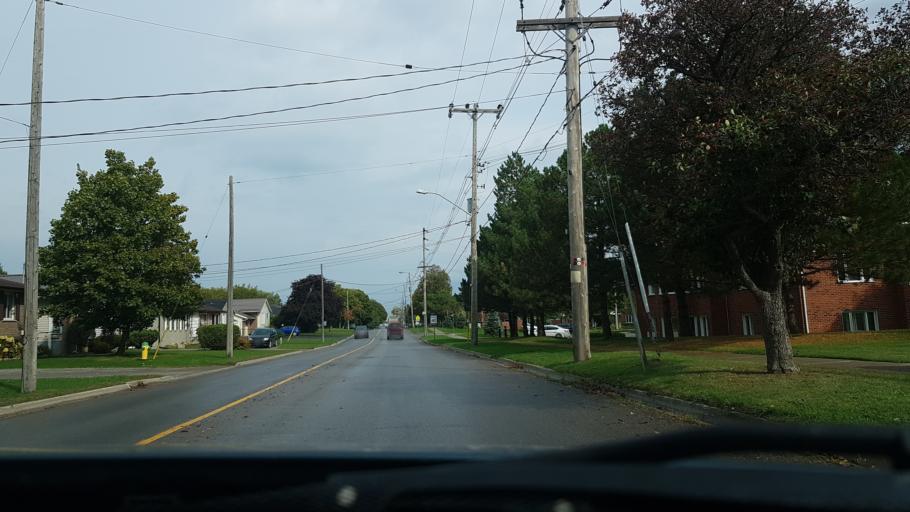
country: CA
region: Ontario
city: Omemee
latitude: 44.3562
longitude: -78.7588
